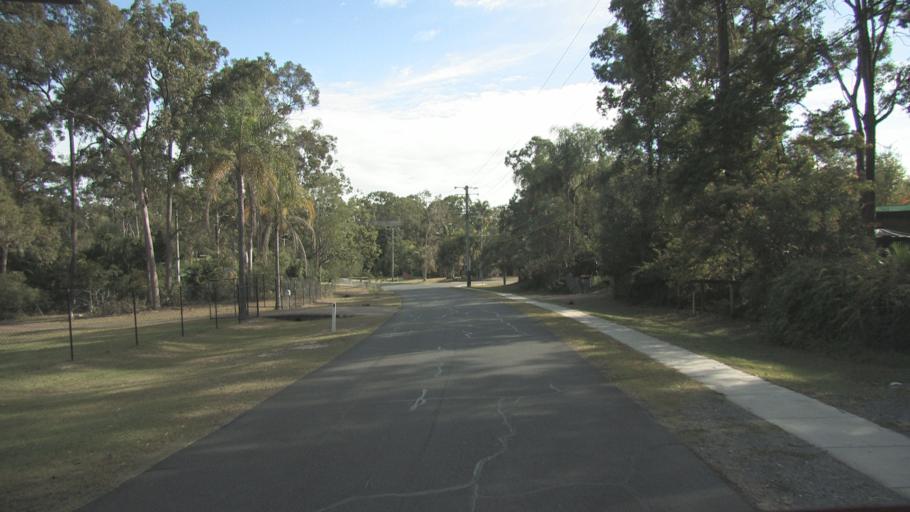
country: AU
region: Queensland
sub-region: Brisbane
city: Forest Lake
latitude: -27.6643
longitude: 153.0028
